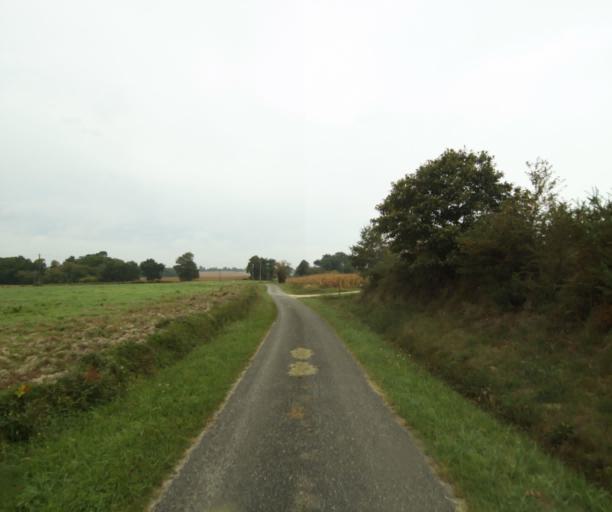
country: FR
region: Midi-Pyrenees
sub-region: Departement du Gers
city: Cazaubon
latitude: 43.9237
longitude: -0.1849
